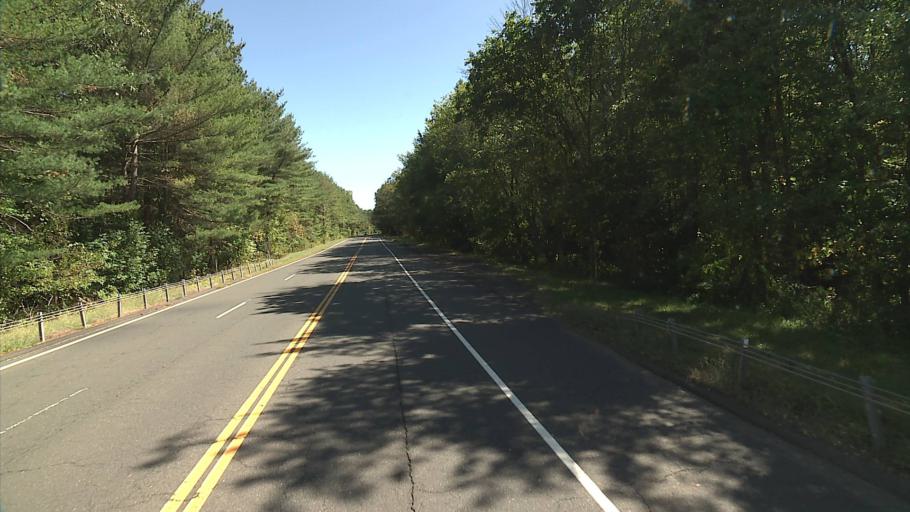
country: US
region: Connecticut
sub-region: New Haven County
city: Cheshire Village
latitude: 41.4983
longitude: -72.8630
